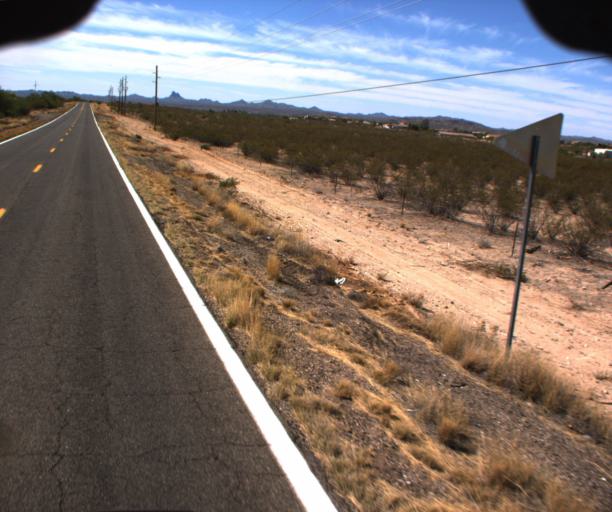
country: US
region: Arizona
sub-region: Yavapai County
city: Congress
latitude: 34.0597
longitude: -112.8183
